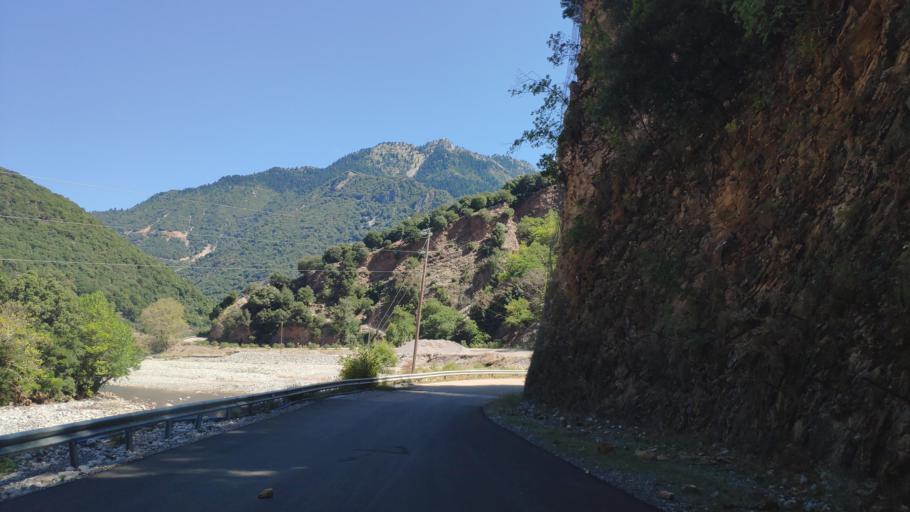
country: GR
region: Central Greece
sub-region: Nomos Evrytanias
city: Kerasochori
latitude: 39.0504
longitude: 21.6008
